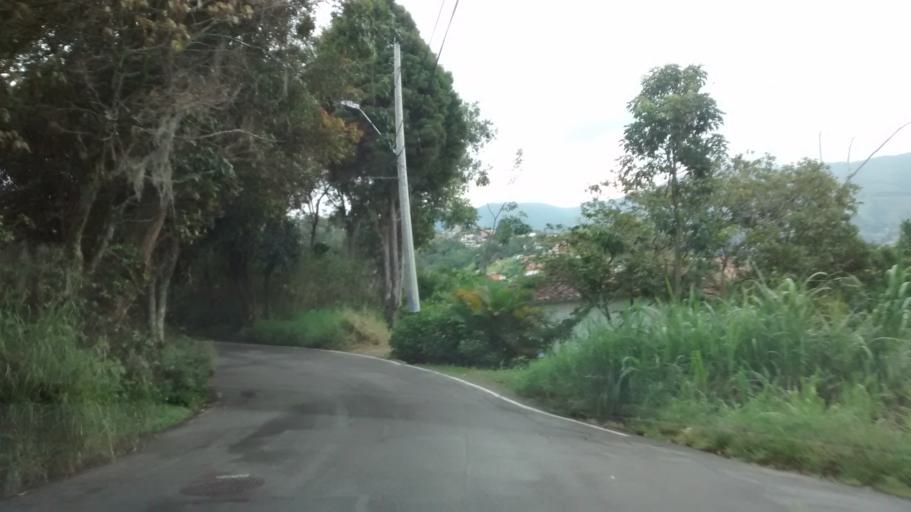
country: CO
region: Antioquia
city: Medellin
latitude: 6.2737
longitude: -75.6294
